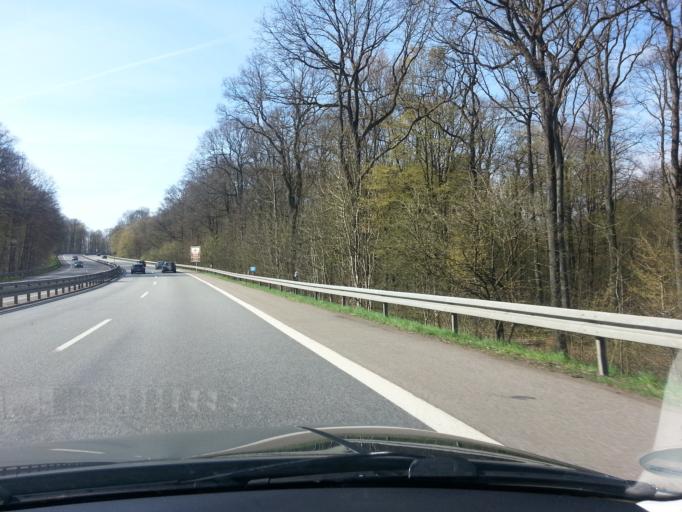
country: DE
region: Saarland
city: Saarbrucken
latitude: 49.2764
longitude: 7.0039
